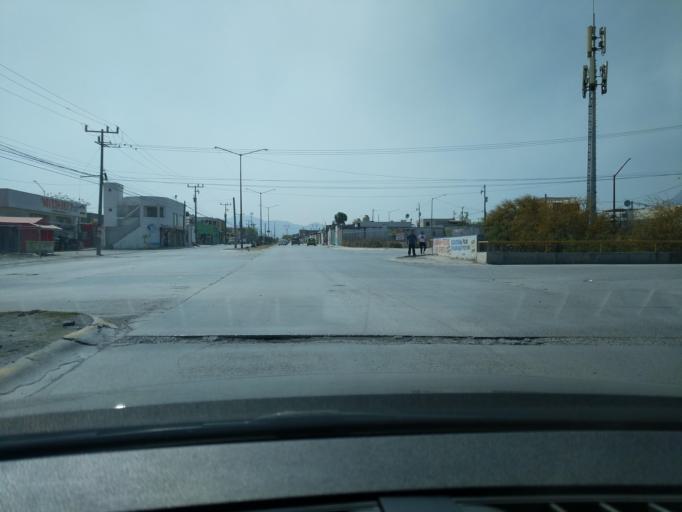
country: MX
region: Nuevo Leon
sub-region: Garcia
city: Valle de Lincoln
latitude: 25.7923
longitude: -100.4801
